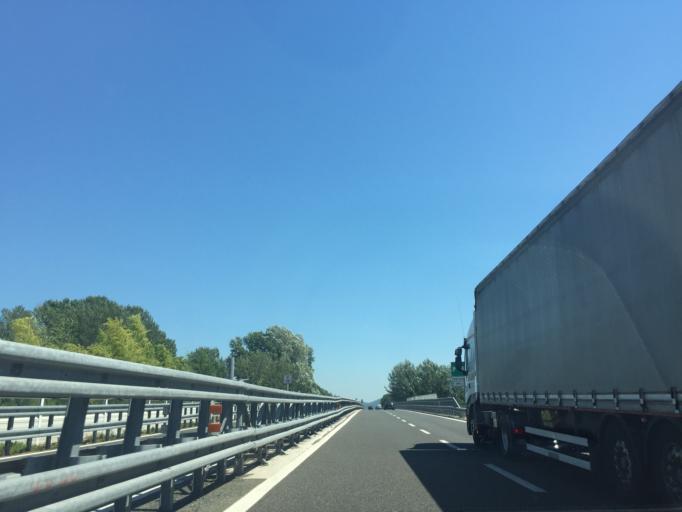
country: IT
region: Tuscany
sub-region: Provincia di Lucca
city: Lucca
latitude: 43.8487
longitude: 10.4442
